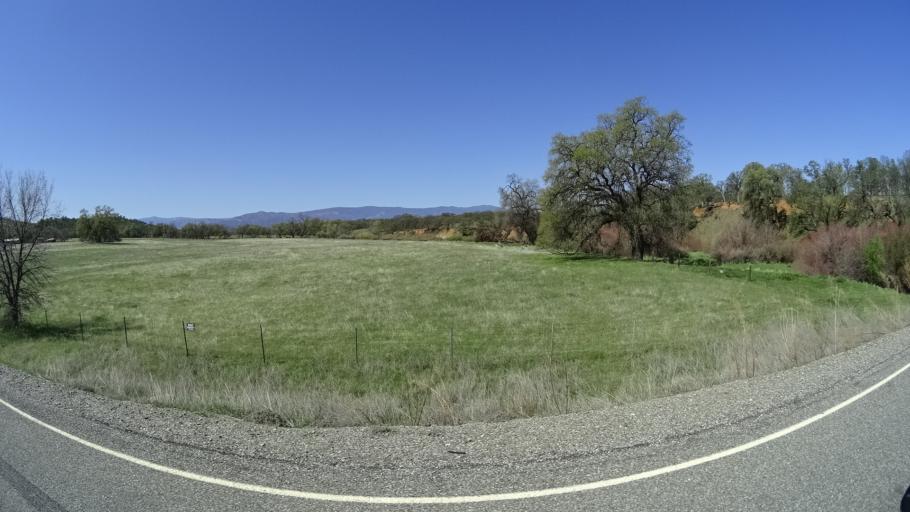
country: US
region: California
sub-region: Tehama County
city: Rancho Tehama Reserve
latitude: 39.8047
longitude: -122.4260
